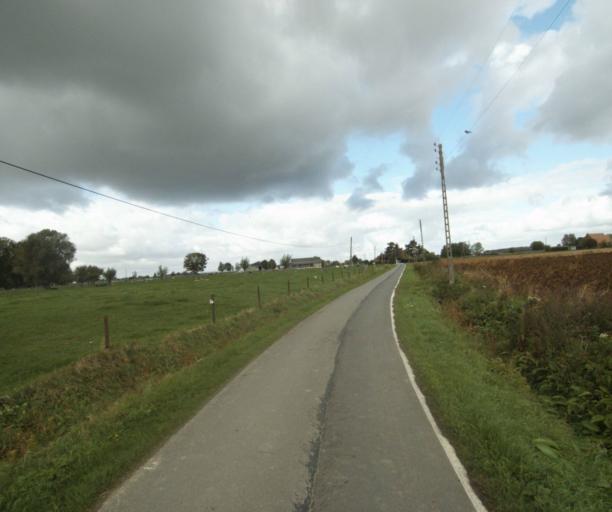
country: FR
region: Nord-Pas-de-Calais
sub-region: Departement du Nord
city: Quesnoy-sur-Deule
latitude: 50.7024
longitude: 2.9789
